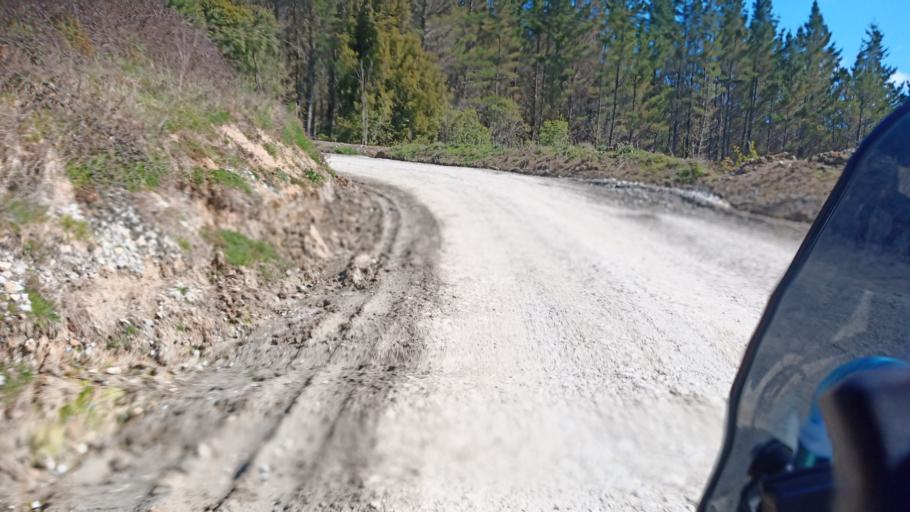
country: NZ
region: Gisborne
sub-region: Gisborne District
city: Gisborne
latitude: -38.8963
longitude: 177.8041
